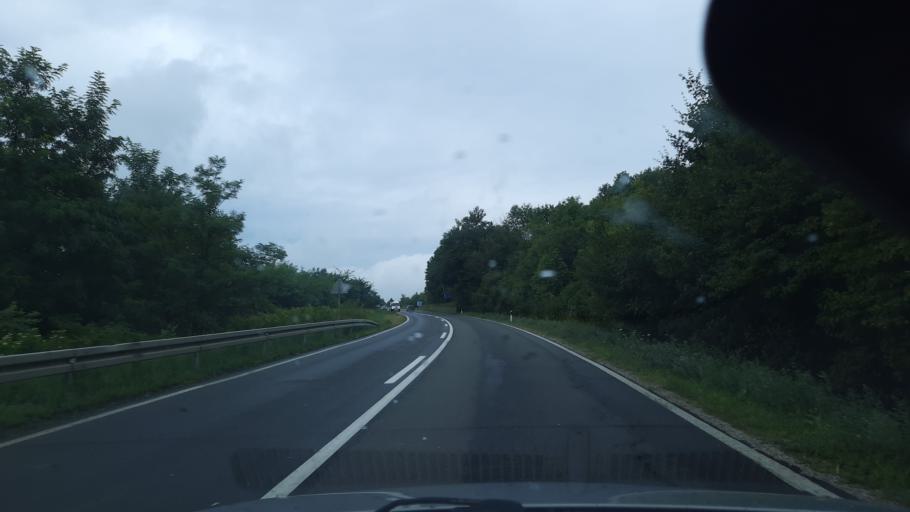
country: RS
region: Central Serbia
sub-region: Sumadijski Okrug
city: Knic
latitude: 43.9540
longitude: 20.8040
